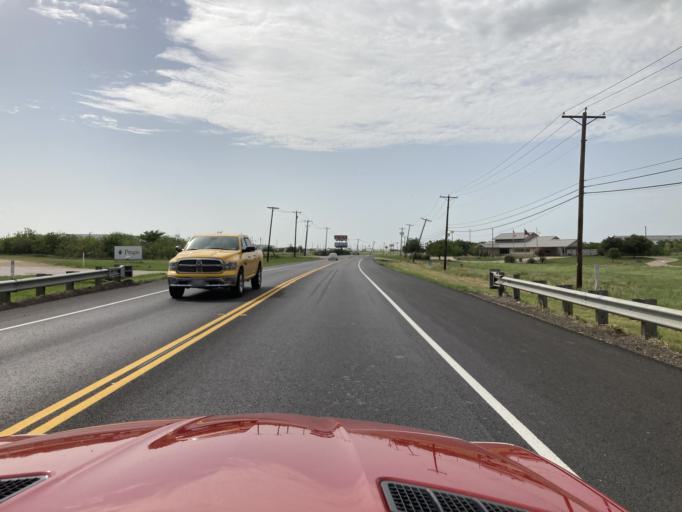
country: US
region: Texas
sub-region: Navarro County
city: Corsicana
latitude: 32.0651
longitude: -96.4380
